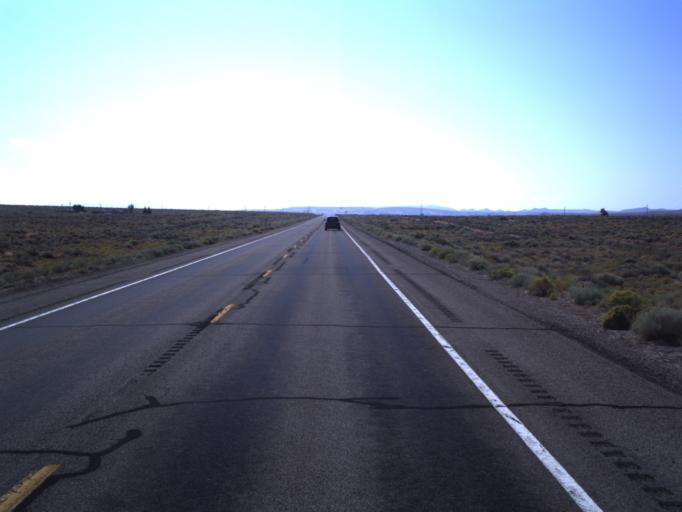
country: US
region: Utah
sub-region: San Juan County
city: Blanding
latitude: 37.1617
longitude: -109.5740
